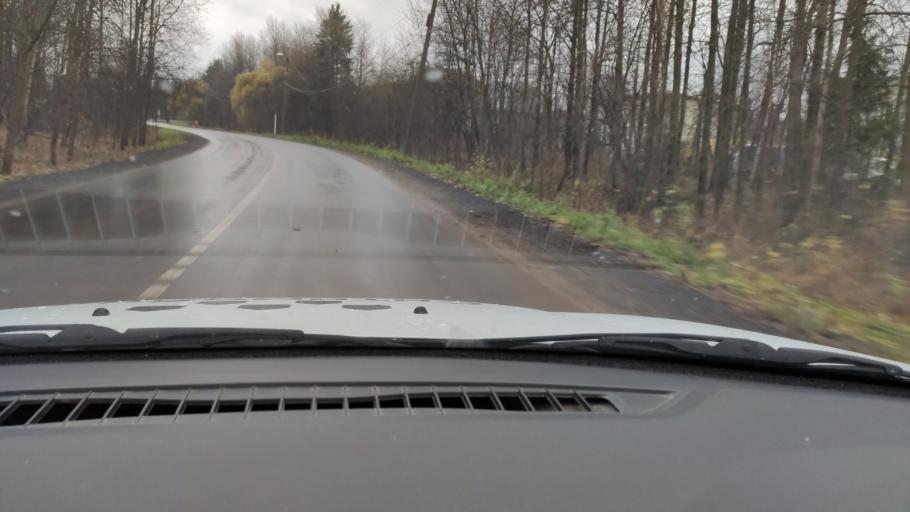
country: RU
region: Perm
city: Sylva
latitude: 58.0339
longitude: 56.7393
